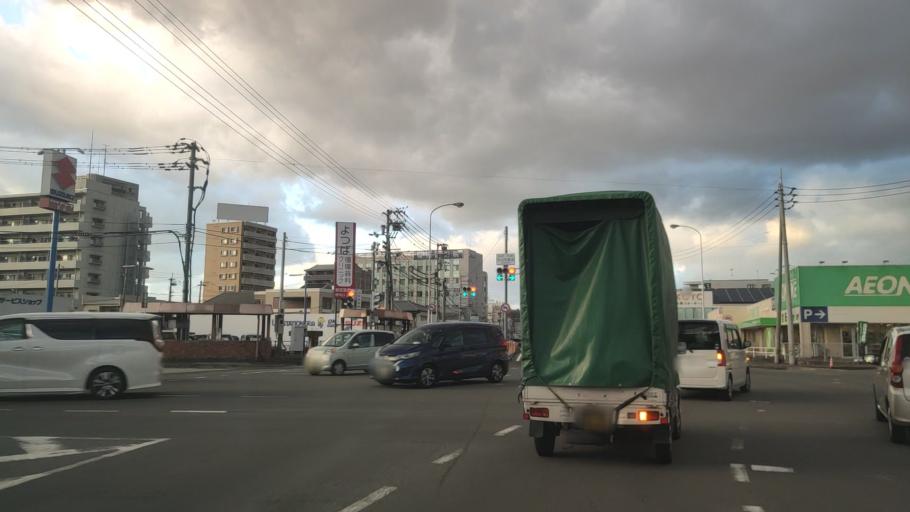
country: JP
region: Ehime
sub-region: Shikoku-chuo Shi
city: Matsuyama
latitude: 33.8221
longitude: 132.7758
